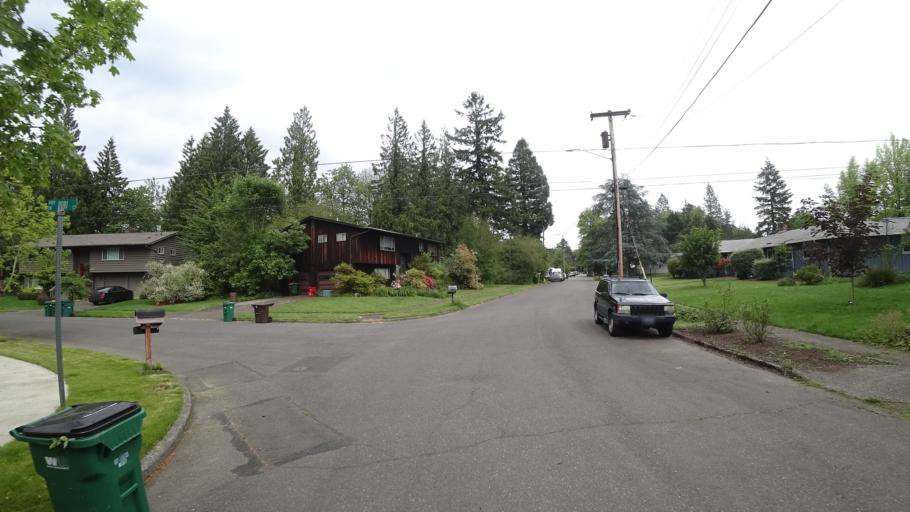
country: US
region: Oregon
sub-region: Washington County
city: Raleigh Hills
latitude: 45.4726
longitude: -122.7822
